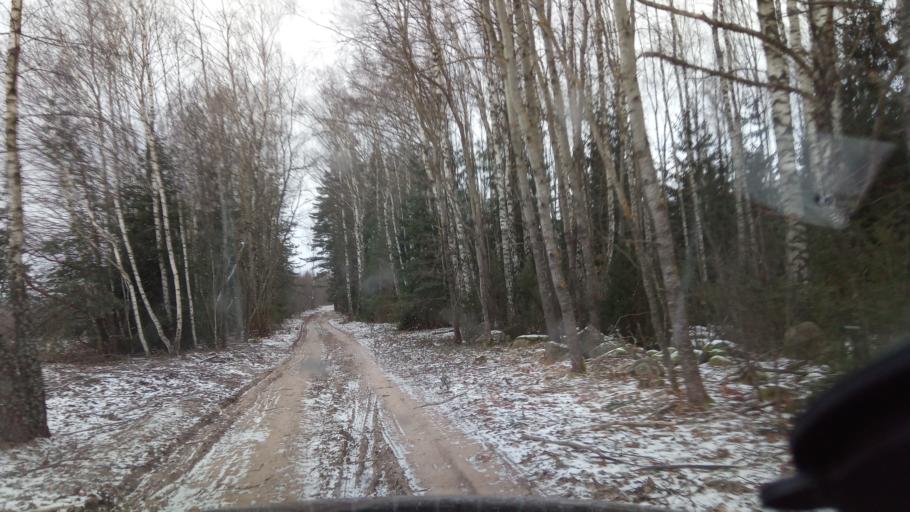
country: LT
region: Alytaus apskritis
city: Varena
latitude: 54.1340
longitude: 24.7011
